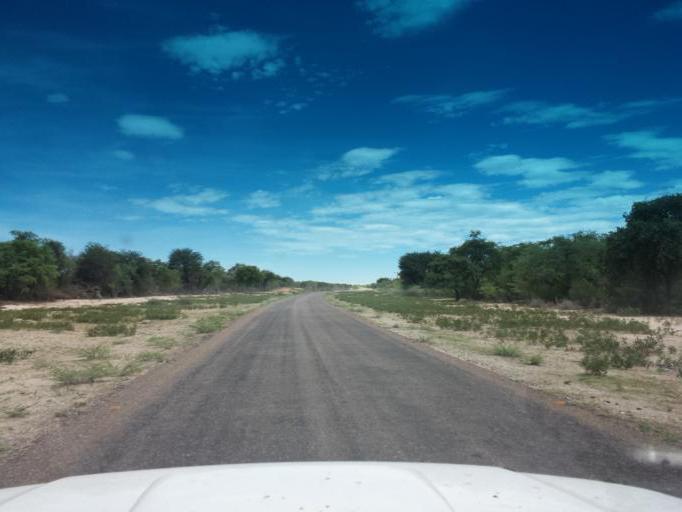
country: BW
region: North West
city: Shakawe
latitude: -18.7127
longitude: 22.1387
